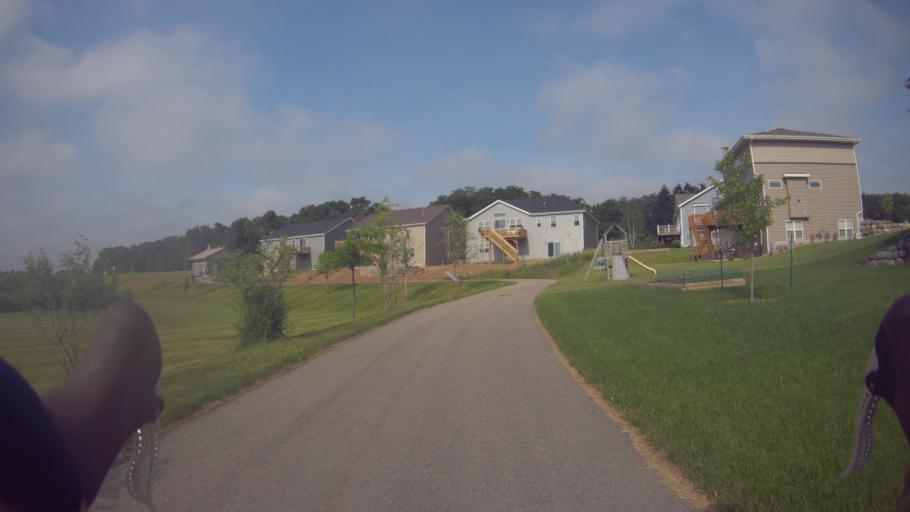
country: US
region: Wisconsin
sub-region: Dane County
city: McFarland
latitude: 43.0199
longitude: -89.2755
